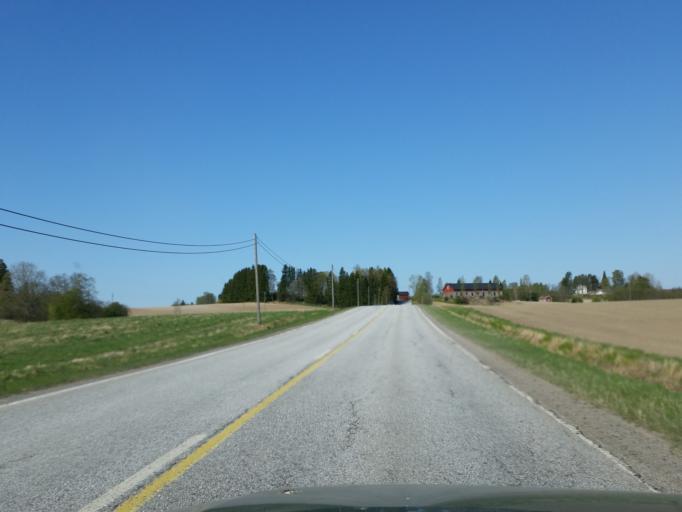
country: FI
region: Uusimaa
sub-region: Helsinki
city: Siuntio
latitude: 60.1754
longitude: 24.1513
